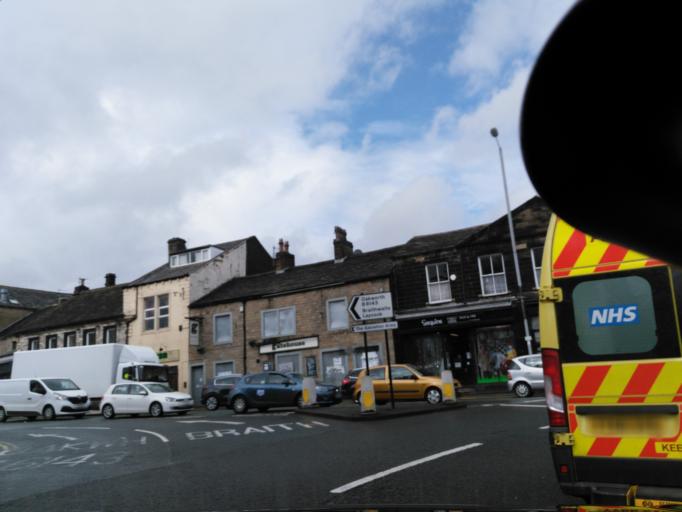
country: GB
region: England
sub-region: Bradford
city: Keighley
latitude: 53.8655
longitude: -1.9110
